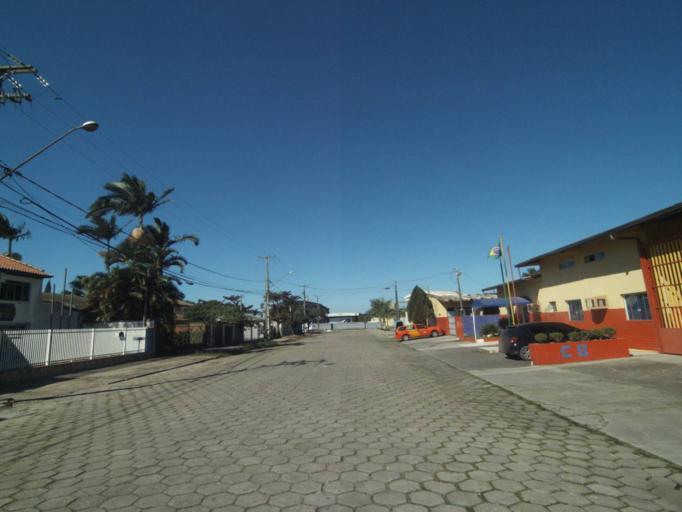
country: BR
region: Parana
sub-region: Paranagua
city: Paranagua
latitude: -25.5135
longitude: -48.5000
